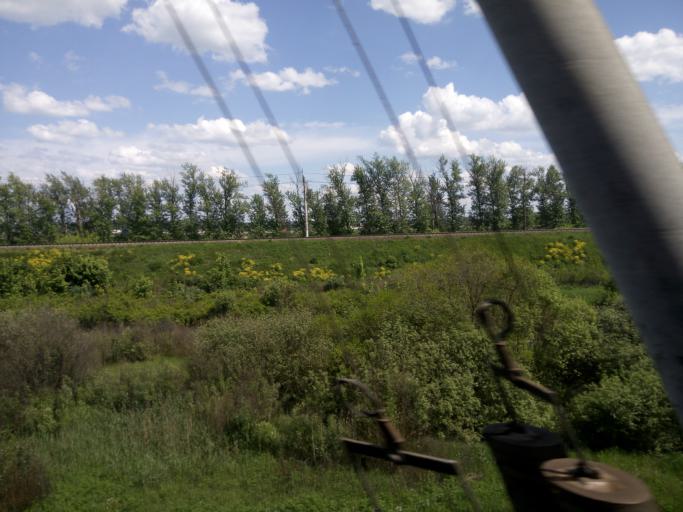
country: RU
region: Moskovskaya
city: Yam
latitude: 55.4927
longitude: 37.7284
